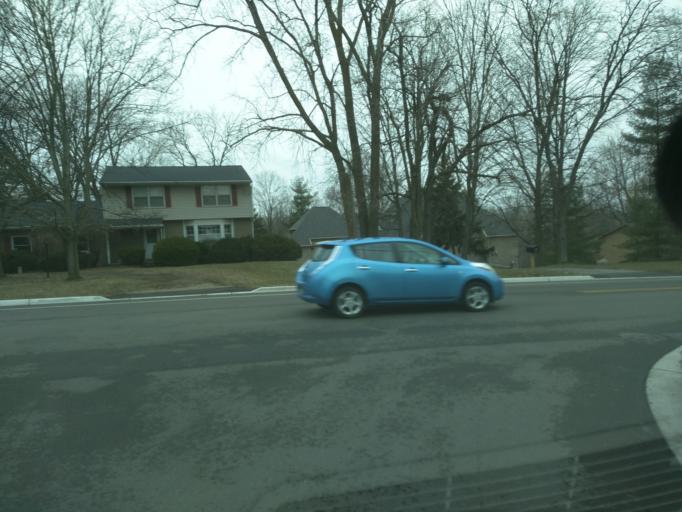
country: US
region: Michigan
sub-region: Eaton County
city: Waverly
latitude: 42.7540
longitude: -84.6126
